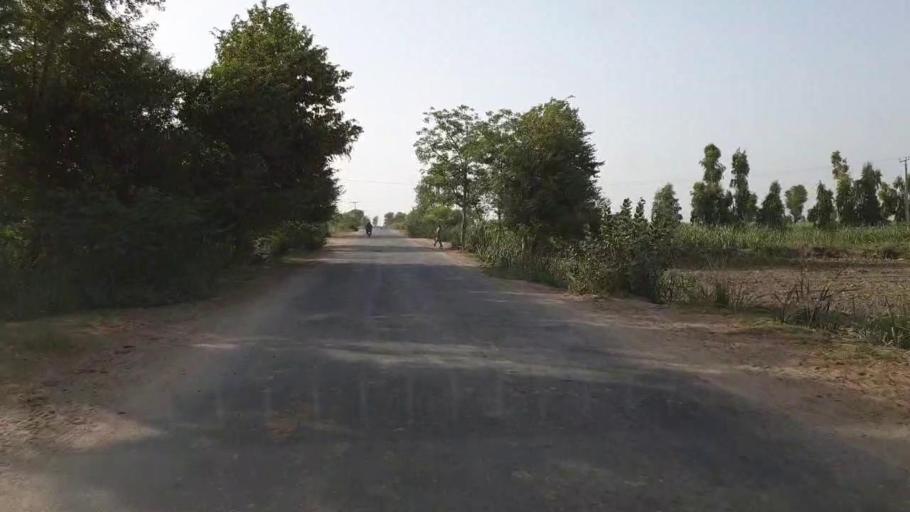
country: PK
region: Sindh
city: Jam Sahib
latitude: 26.3901
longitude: 68.8814
